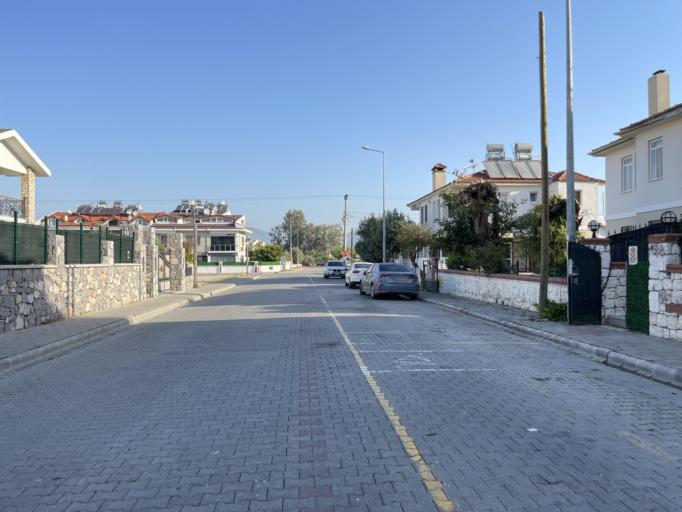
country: TR
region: Mugla
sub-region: Fethiye
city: Fethiye
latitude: 36.6578
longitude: 29.1229
